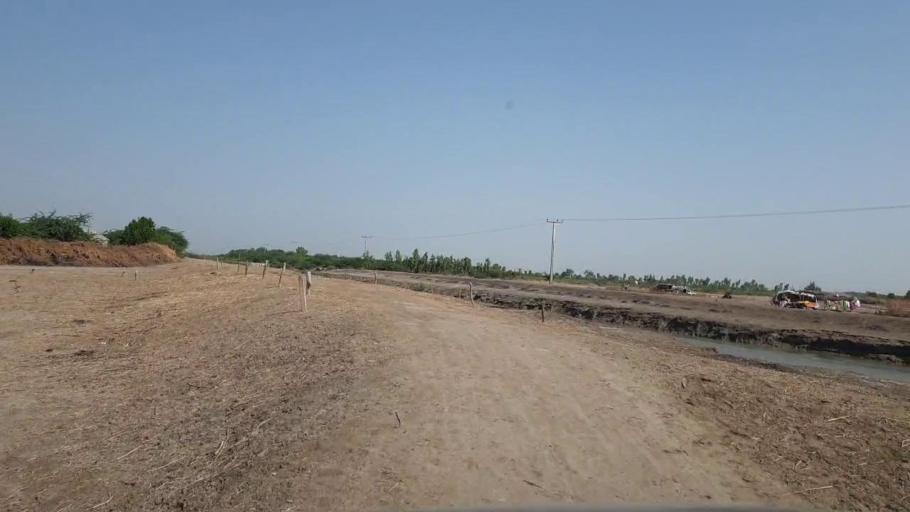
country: PK
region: Sindh
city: Tando Bago
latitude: 24.6961
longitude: 69.0701
